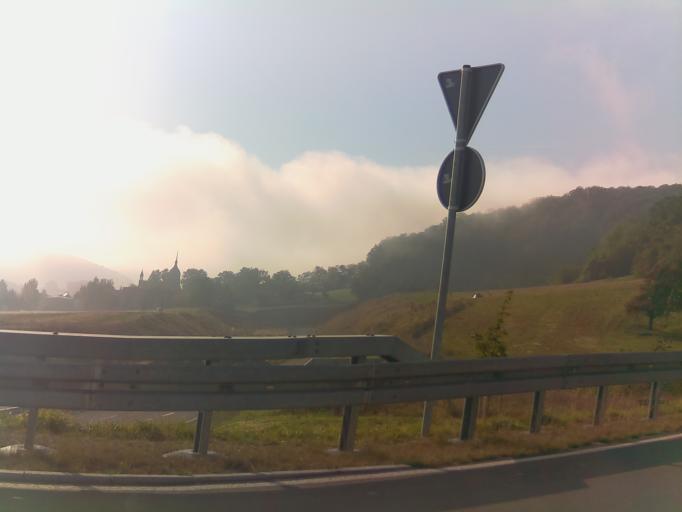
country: DE
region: Thuringia
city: Rothenstein
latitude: 50.8535
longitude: 11.5970
